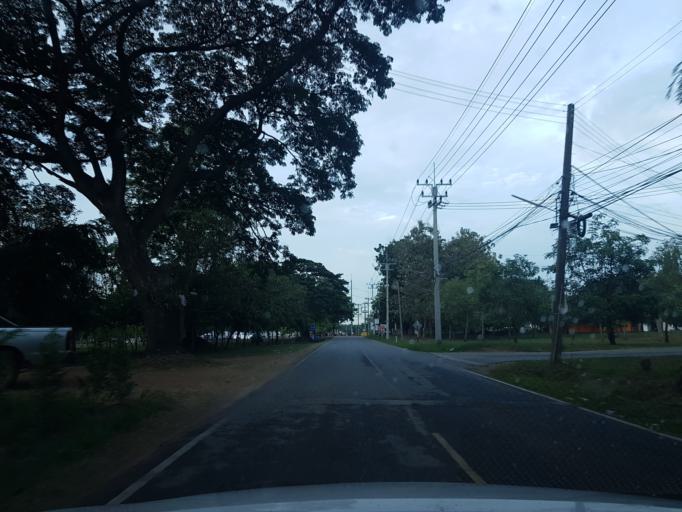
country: TH
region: Sara Buri
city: Muak Lek
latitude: 14.6341
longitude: 101.2026
